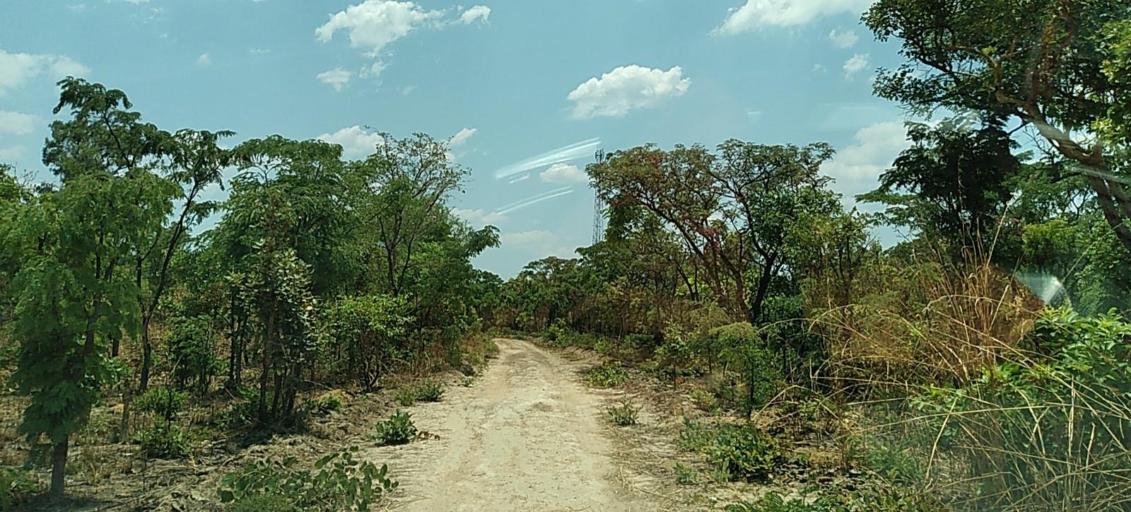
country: ZM
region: Copperbelt
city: Chililabombwe
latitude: -12.4506
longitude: 27.6787
